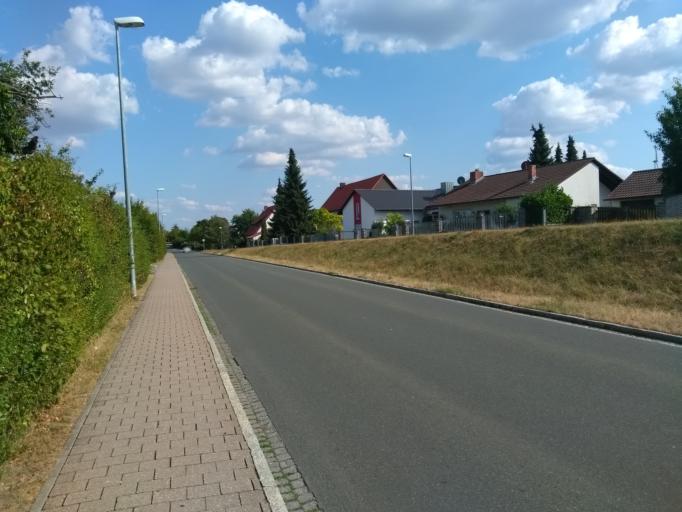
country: DE
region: Bavaria
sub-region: Regierungsbezirk Mittelfranken
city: Hagenbuchach
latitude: 49.5358
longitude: 10.7685
